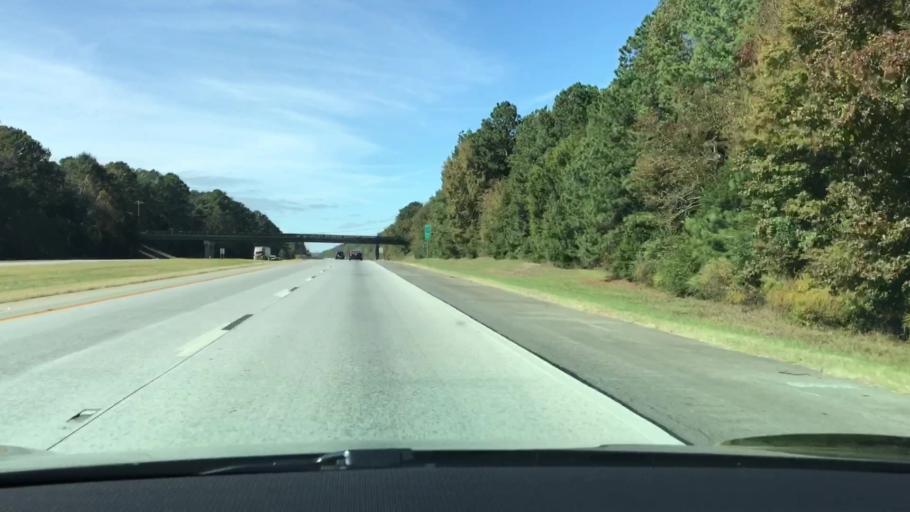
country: US
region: Georgia
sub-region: Morgan County
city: Madison
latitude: 33.5552
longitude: -83.4293
